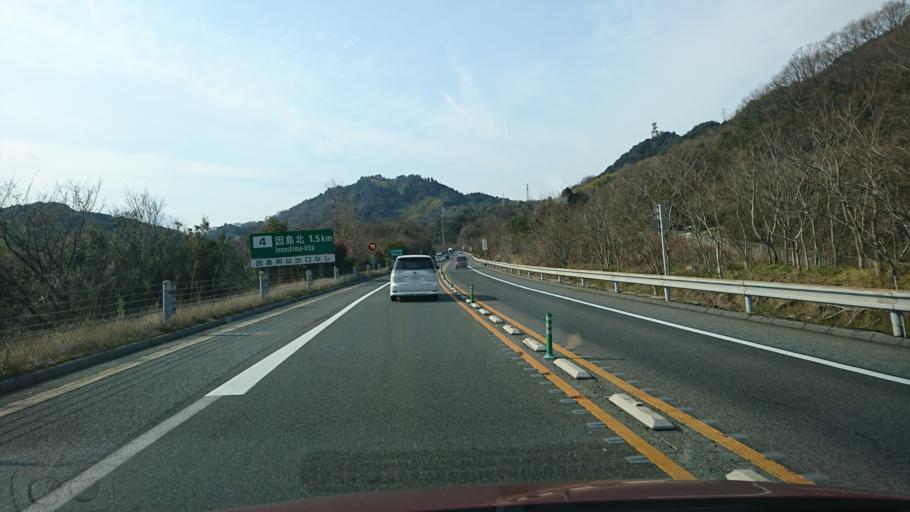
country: JP
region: Hiroshima
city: Innoshima
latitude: 34.3500
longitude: 133.1676
